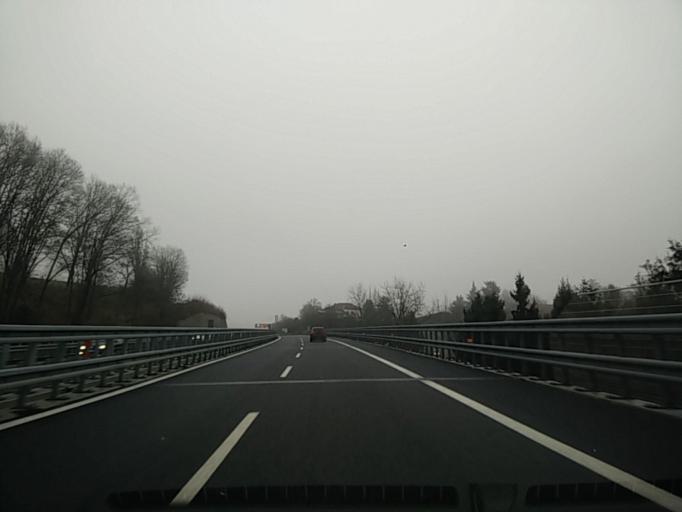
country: IT
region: Piedmont
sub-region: Provincia di Asti
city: Asti
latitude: 44.9156
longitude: 8.2115
